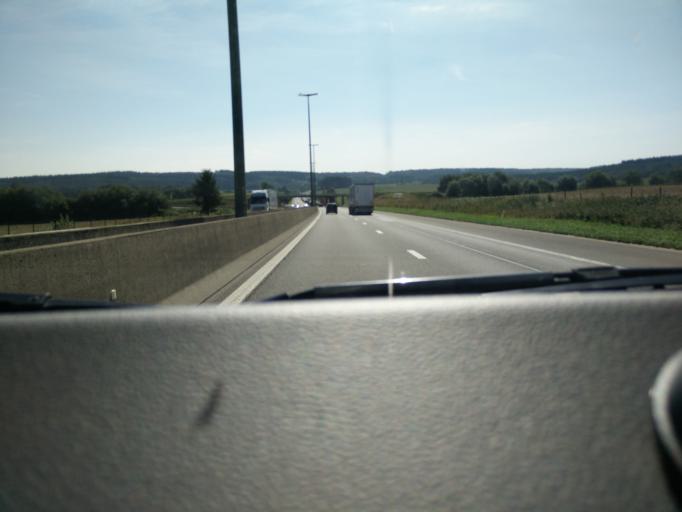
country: BE
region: Wallonia
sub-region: Province du Luxembourg
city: Leglise
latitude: 49.7778
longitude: 5.5422
